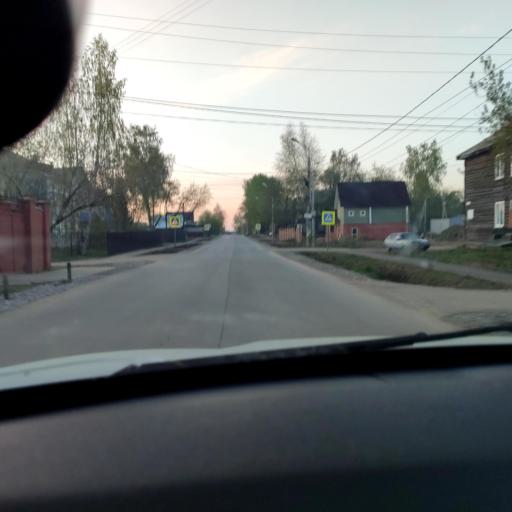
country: RU
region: Perm
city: Krasnokamsk
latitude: 58.0593
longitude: 55.8044
